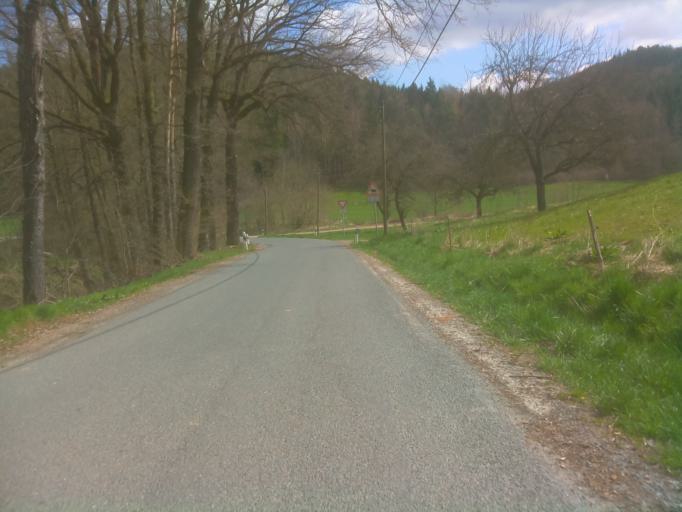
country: DE
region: Thuringia
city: Weissbach
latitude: 50.8064
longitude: 11.7875
